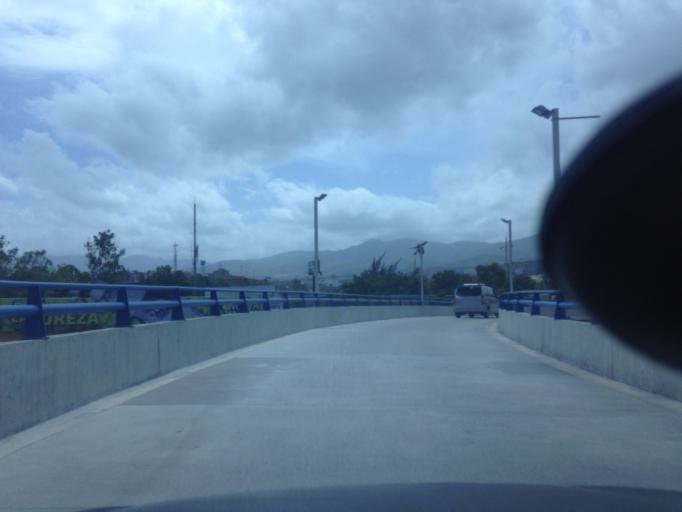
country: HN
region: Francisco Morazan
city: Tegucigalpa
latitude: 14.0725
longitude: -87.2136
